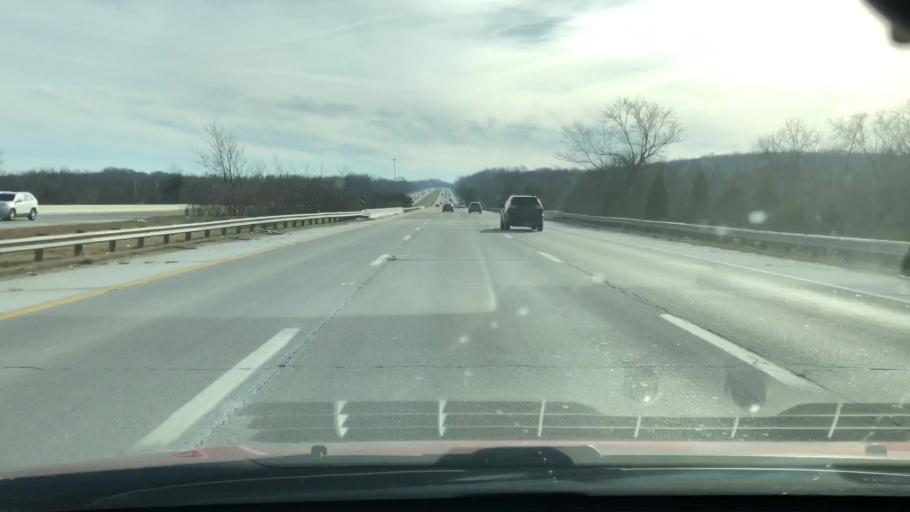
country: US
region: Ohio
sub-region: Greene County
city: Beavercreek
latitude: 39.7268
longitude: -84.0908
